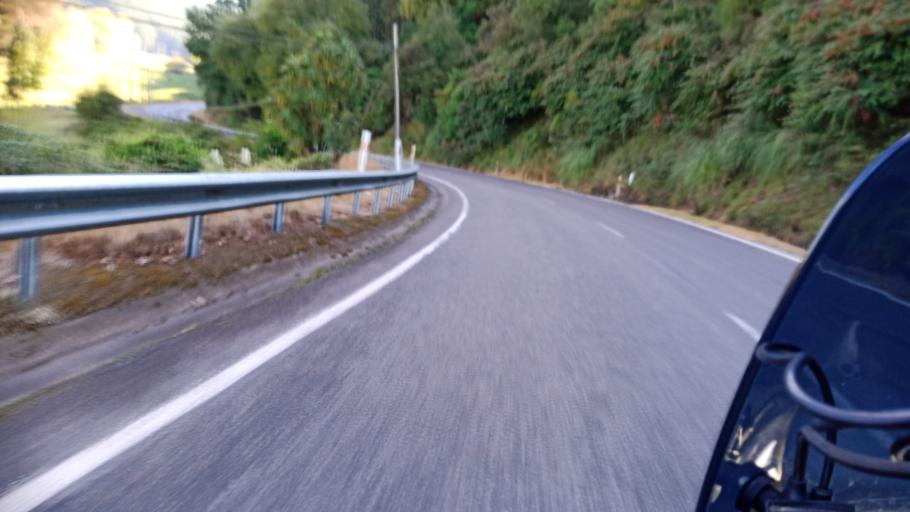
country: NZ
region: Hawke's Bay
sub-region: Wairoa District
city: Wairoa
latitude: -38.9257
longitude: 177.2737
